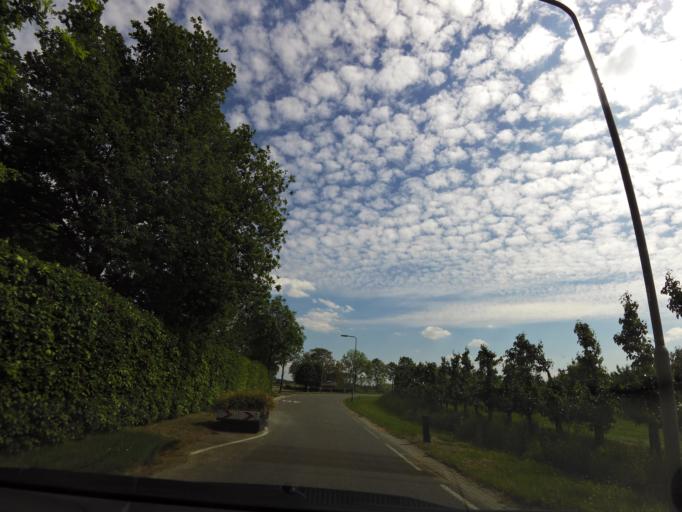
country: NL
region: Limburg
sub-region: Gemeente Roerdalen
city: Sint Odilienberg
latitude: 51.1658
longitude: 5.9913
